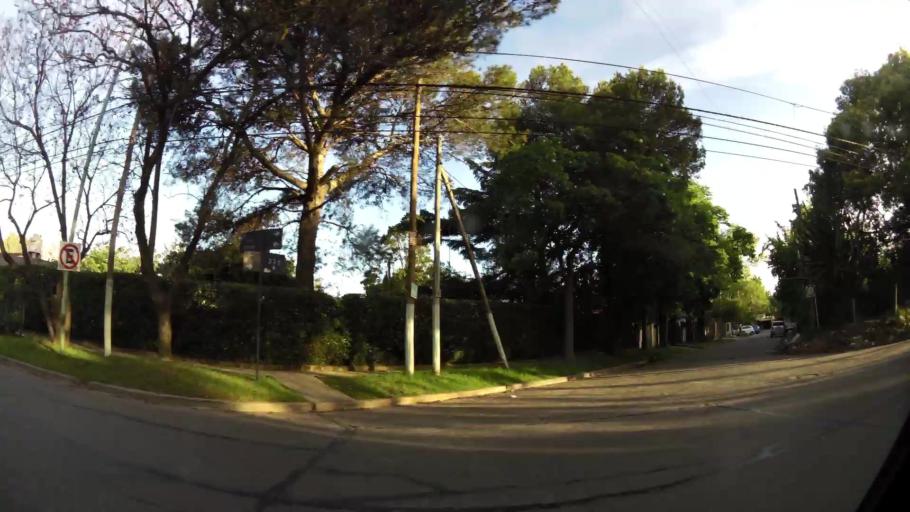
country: AR
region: Buenos Aires
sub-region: Partido de Quilmes
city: Quilmes
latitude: -34.7802
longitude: -58.1997
